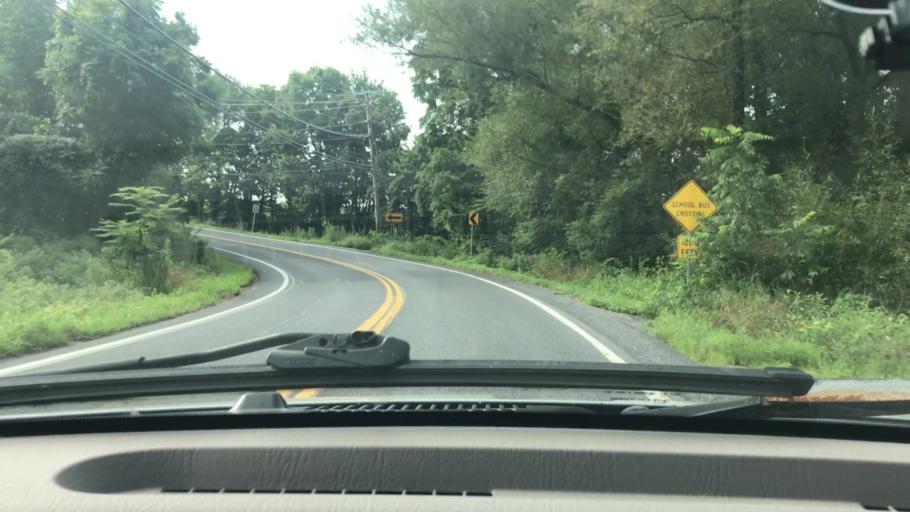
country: US
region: Pennsylvania
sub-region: Dauphin County
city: Middletown
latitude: 40.2154
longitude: -76.7425
